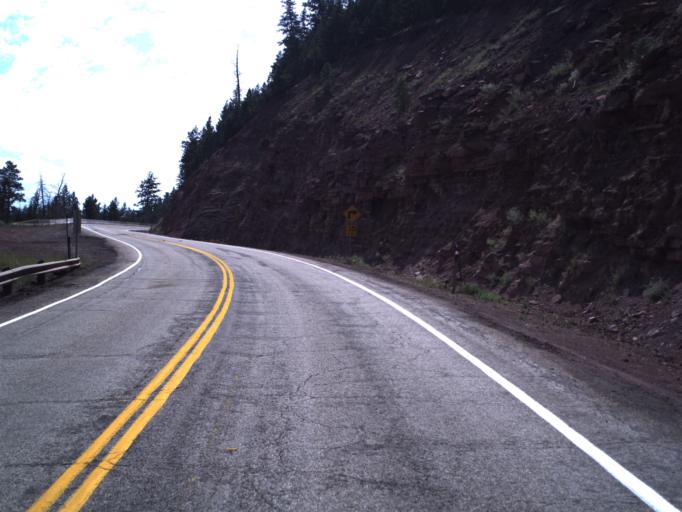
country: US
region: Utah
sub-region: Daggett County
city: Manila
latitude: 40.8669
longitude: -109.6876
